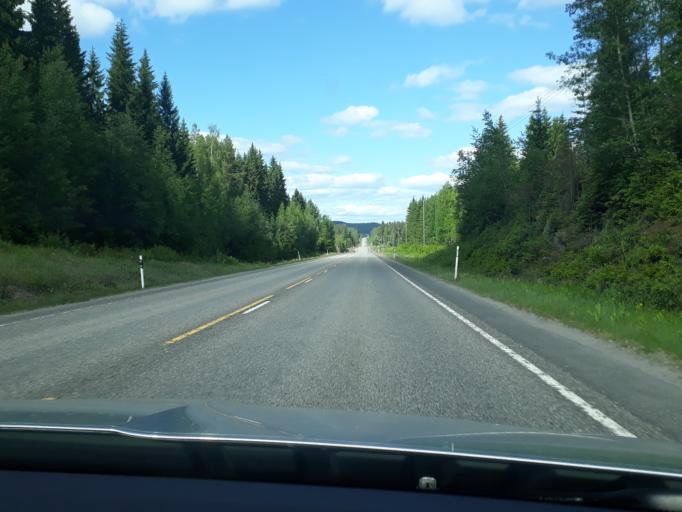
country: FI
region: Central Finland
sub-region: AEaenekoski
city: AEaenekoski
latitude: 62.6507
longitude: 25.7169
